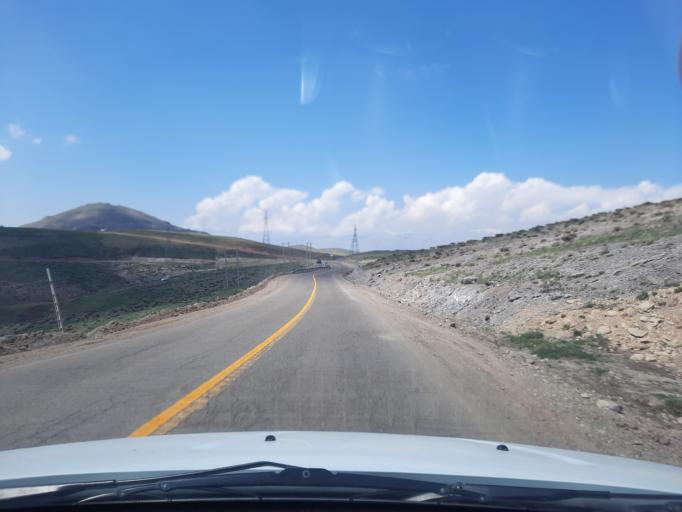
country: IR
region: Qazvin
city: Qazvin
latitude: 36.3906
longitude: 50.2082
